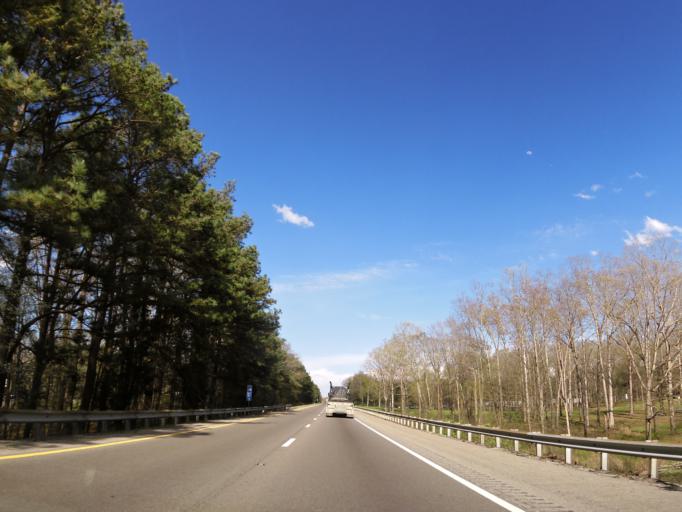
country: US
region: Tennessee
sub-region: Dickson County
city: Dickson
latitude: 36.0103
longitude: -87.3824
